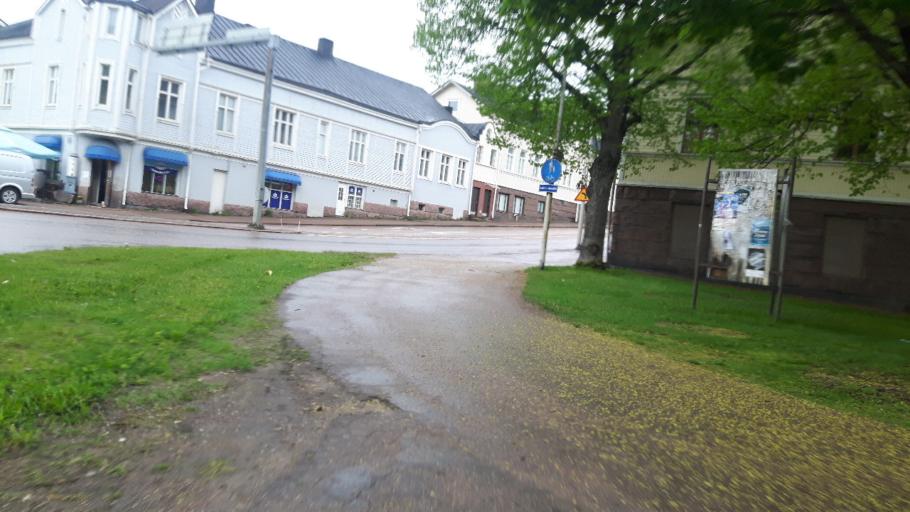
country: FI
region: Kymenlaakso
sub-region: Kotka-Hamina
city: Kotka
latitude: 60.4714
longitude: 26.9227
